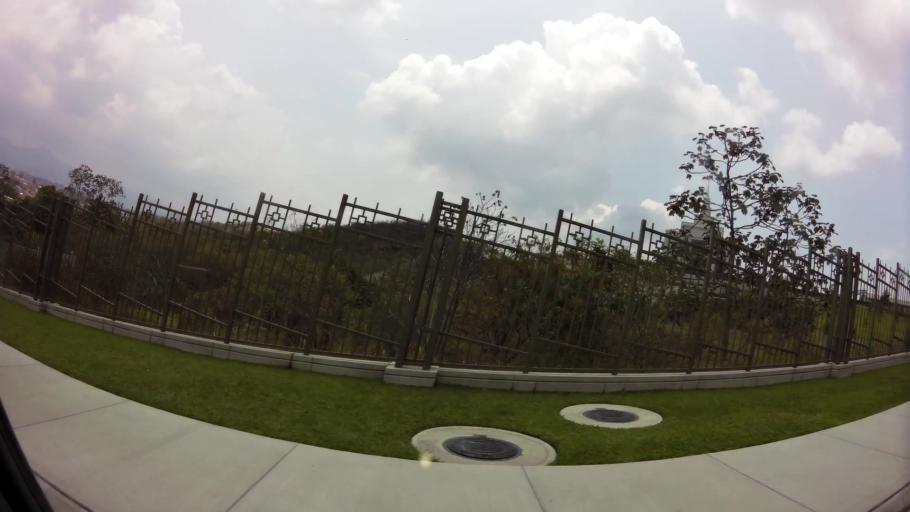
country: HN
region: Francisco Morazan
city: Tegucigalpa
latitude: 14.0538
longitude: -87.2382
